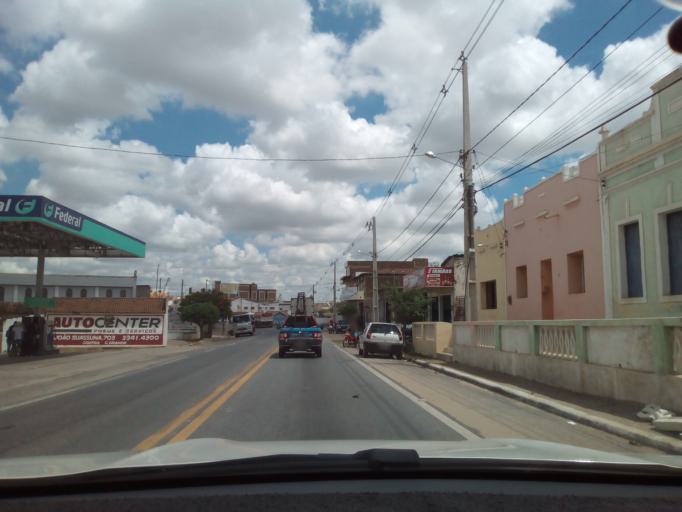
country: BR
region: Paraiba
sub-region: Soledade
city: Soledade
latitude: -7.0579
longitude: -36.3590
